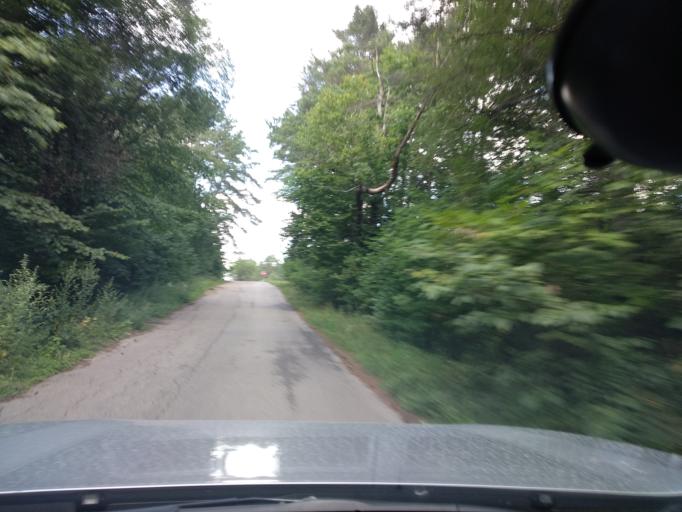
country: LT
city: Grigiskes
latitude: 54.6812
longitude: 25.0789
